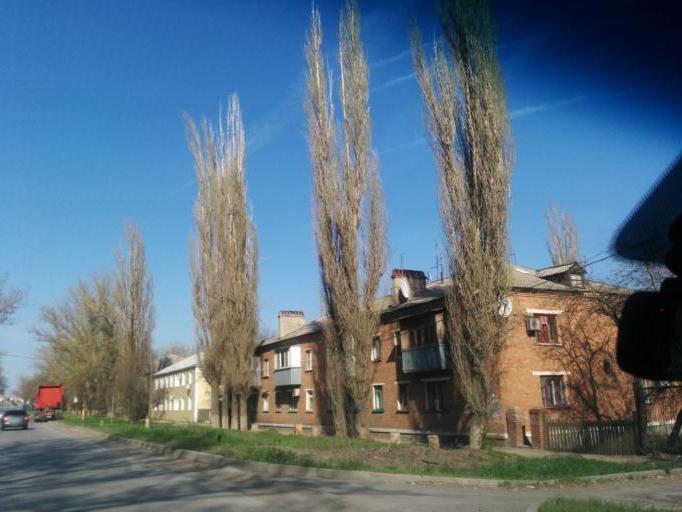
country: RU
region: Rostov
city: Shakhty
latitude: 47.7007
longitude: 40.1962
